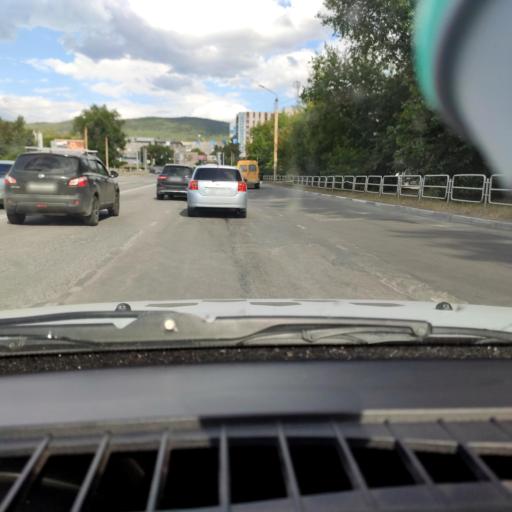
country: RU
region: Chelyabinsk
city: Miass
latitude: 55.0645
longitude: 60.1047
